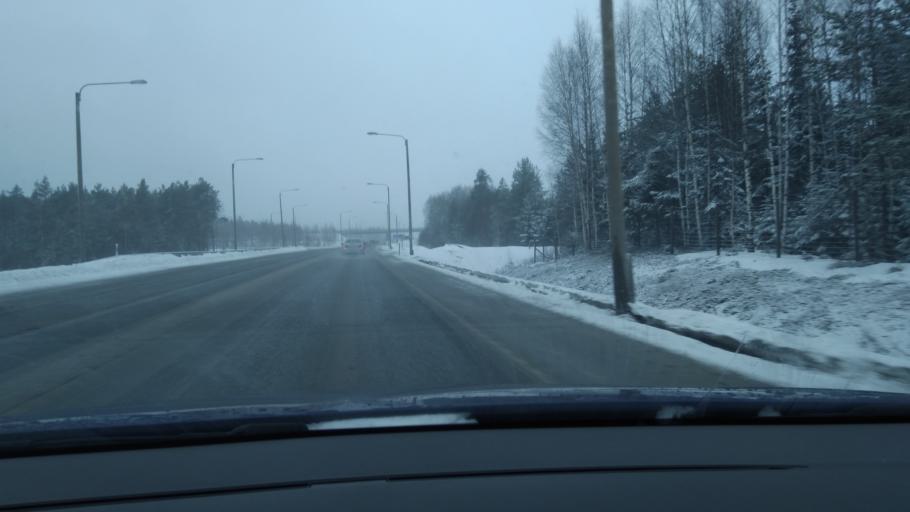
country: FI
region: Pirkanmaa
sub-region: Tampere
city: Kangasala
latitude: 61.5372
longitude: 23.9877
